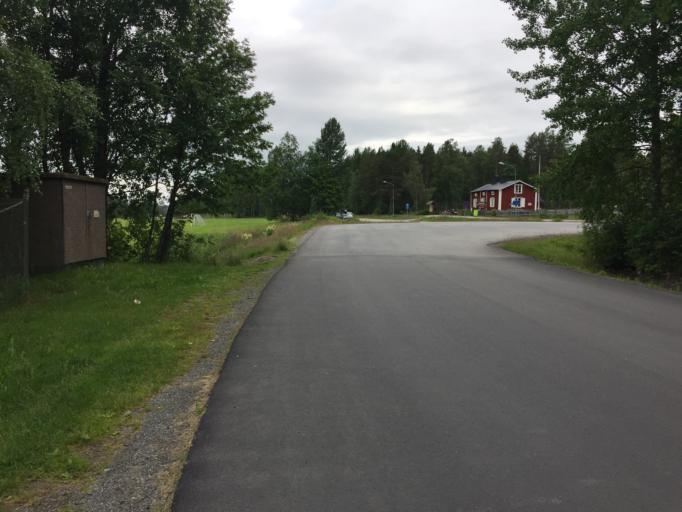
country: SE
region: Vaesterbotten
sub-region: Umea Kommun
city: Ersmark
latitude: 63.8423
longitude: 20.3402
